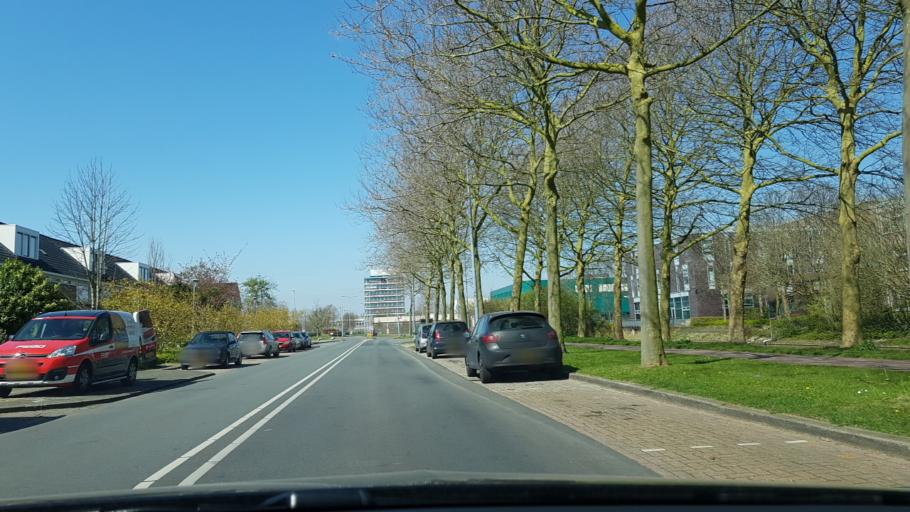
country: NL
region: South Holland
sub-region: Gemeente Hillegom
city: Hillegom
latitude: 52.2710
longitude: 4.6336
